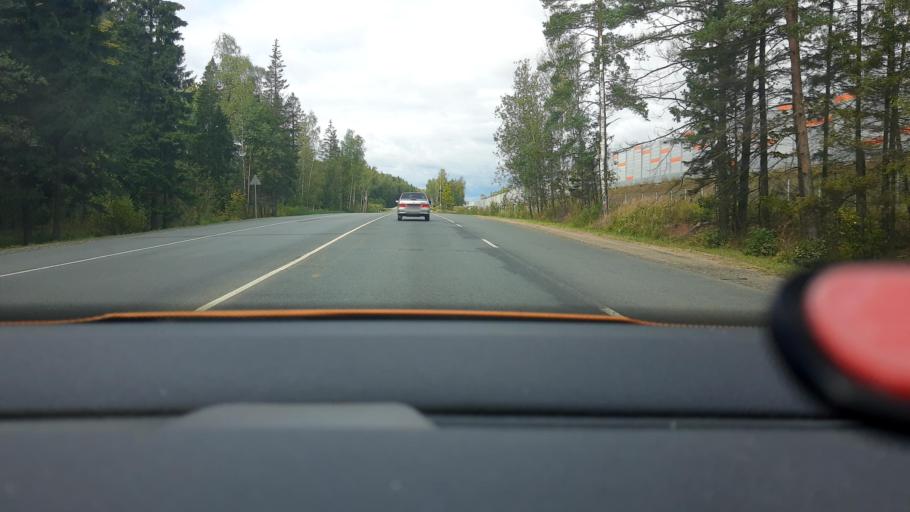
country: RU
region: Moskovskaya
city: Zelenogradskiy
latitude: 56.0865
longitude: 37.9966
